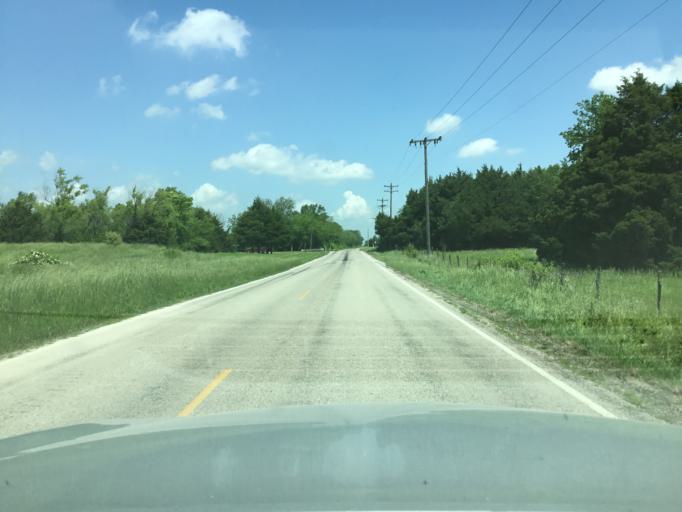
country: US
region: Kansas
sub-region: Labette County
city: Parsons
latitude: 37.3460
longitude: -95.3038
